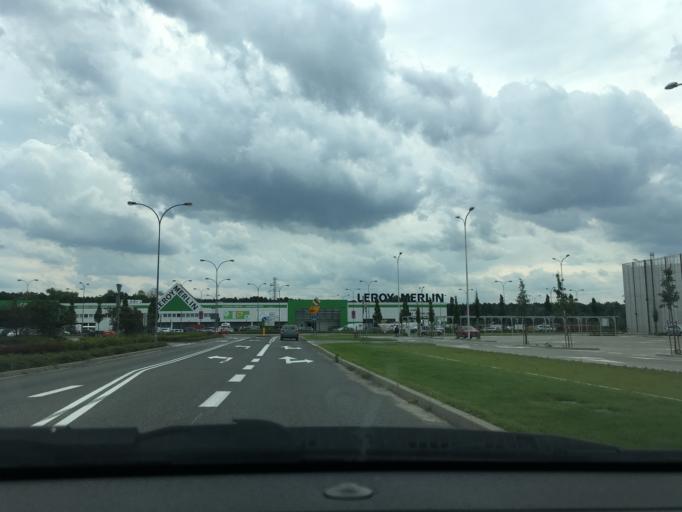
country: PL
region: Masovian Voivodeship
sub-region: Warszawa
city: Targowek
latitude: 52.3052
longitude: 21.0758
